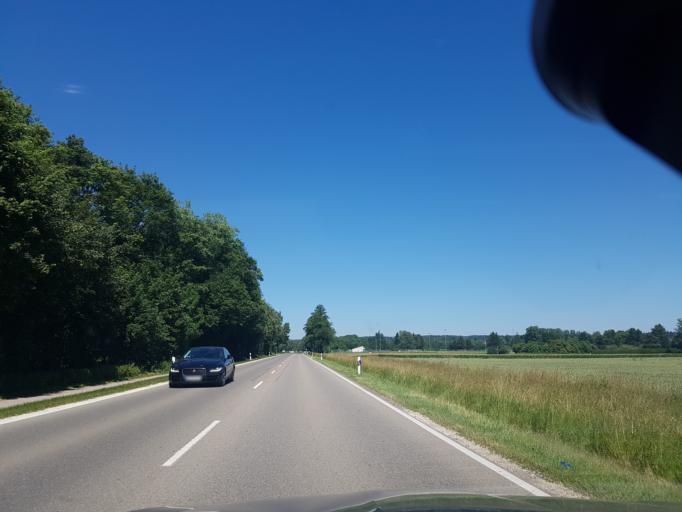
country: DE
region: Bavaria
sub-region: Swabia
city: Weissenhorn
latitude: 48.2966
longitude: 10.1434
